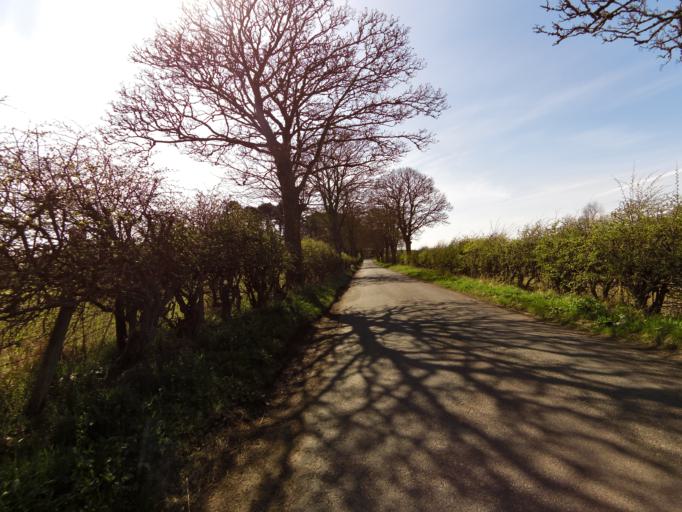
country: GB
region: Scotland
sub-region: Angus
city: Montrose
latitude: 56.6529
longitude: -2.5110
